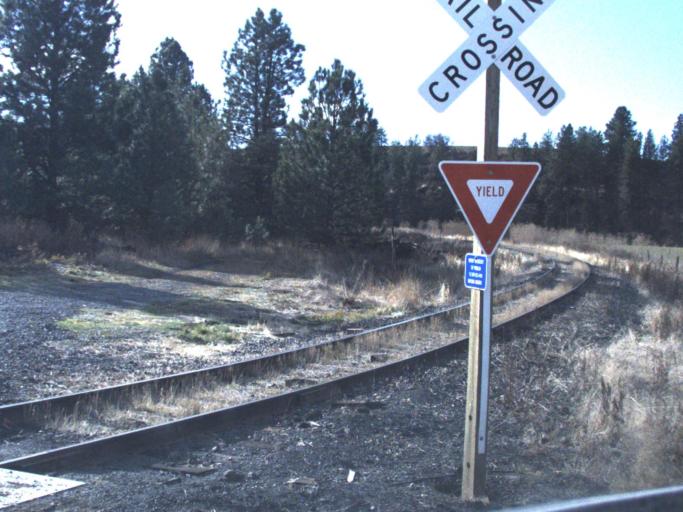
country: US
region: Idaho
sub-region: Latah County
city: Moscow
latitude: 46.9134
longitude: -117.0875
